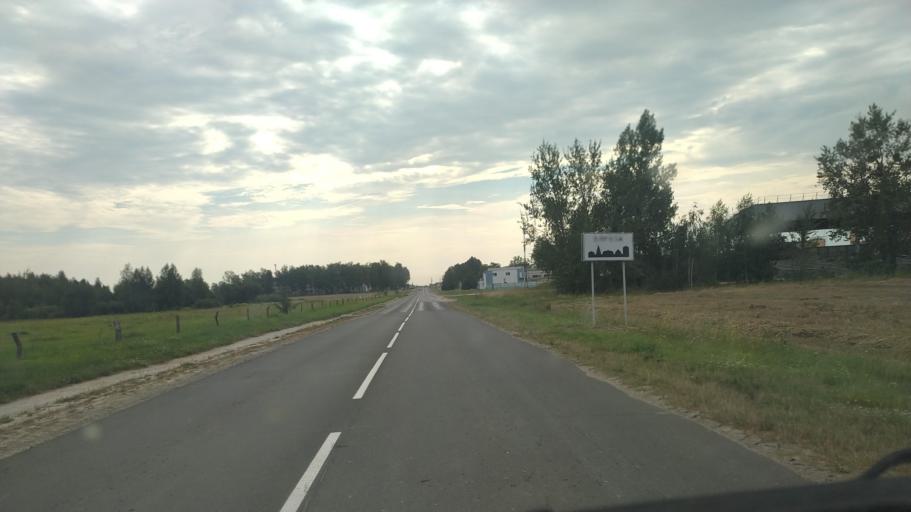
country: BY
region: Brest
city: Byaroza
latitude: 52.5532
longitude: 24.9298
